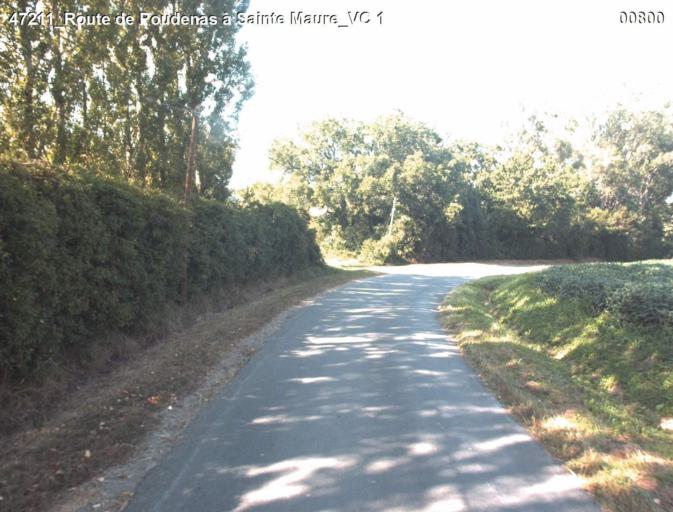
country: FR
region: Aquitaine
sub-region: Departement du Lot-et-Garonne
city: Mezin
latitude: 44.0407
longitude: 0.2095
